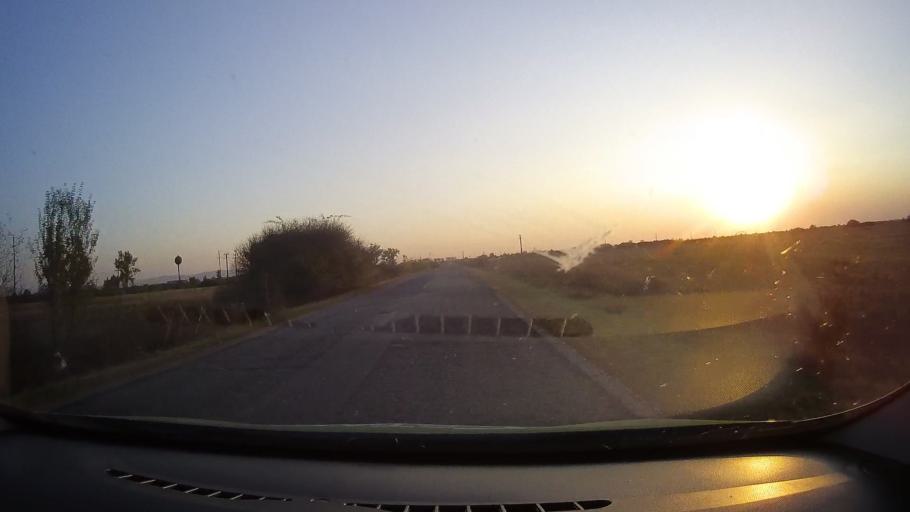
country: RO
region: Arad
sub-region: Comuna Seleus
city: Seleus
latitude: 46.3926
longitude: 21.7142
